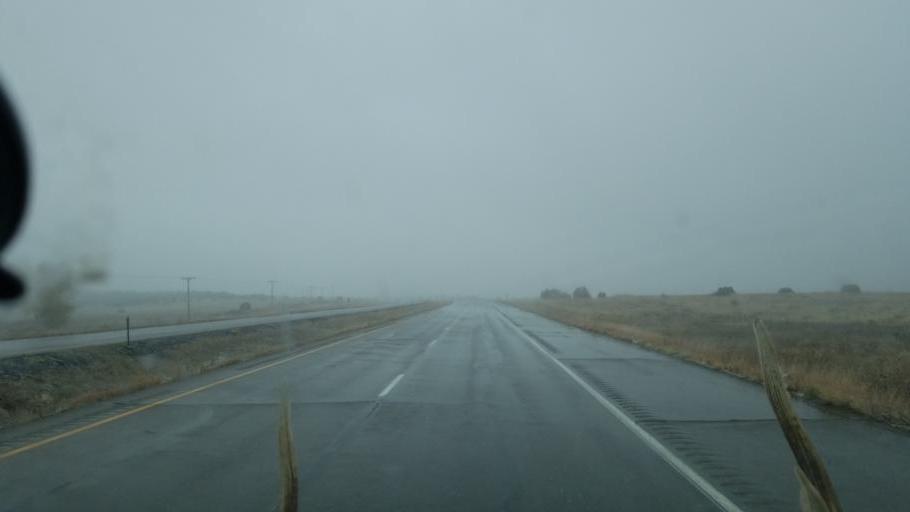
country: US
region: Colorado
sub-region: Pueblo County
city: Colorado City
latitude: 38.0258
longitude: -104.7341
